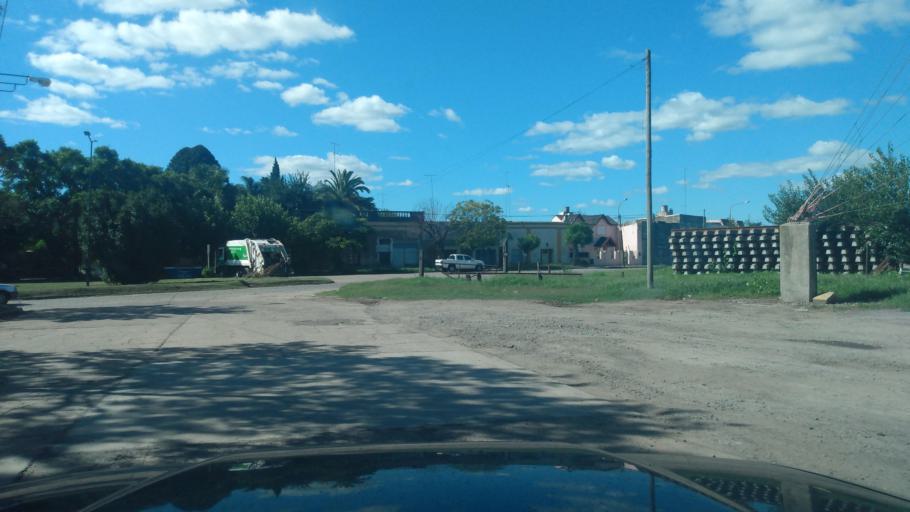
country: AR
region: Buenos Aires
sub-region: Partido de Lujan
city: Lujan
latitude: -34.5773
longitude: -59.1050
